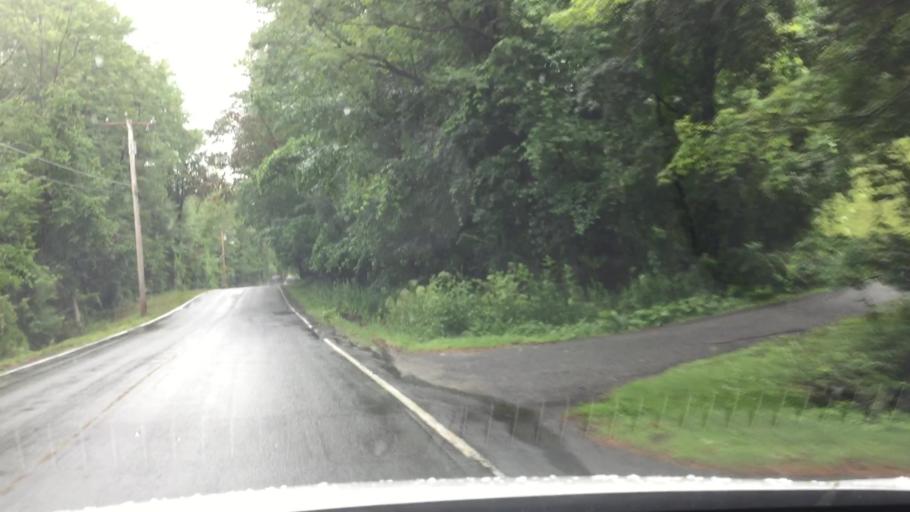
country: US
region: Massachusetts
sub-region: Berkshire County
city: Pittsfield
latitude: 42.4194
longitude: -73.2837
